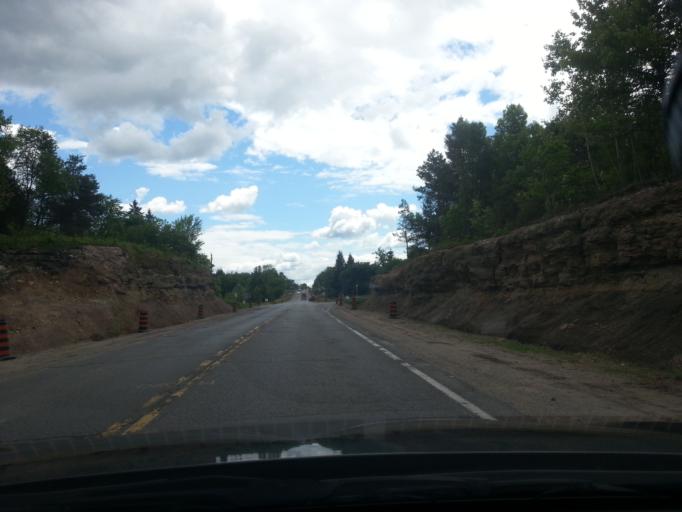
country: CA
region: Ontario
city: Gananoque
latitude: 44.6071
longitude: -76.2250
